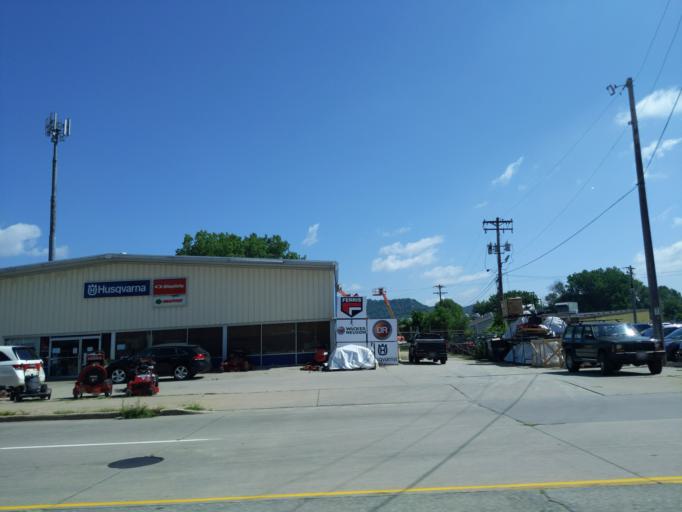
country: US
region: Wisconsin
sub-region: La Crosse County
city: La Crosse
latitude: 43.7811
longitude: -91.2265
